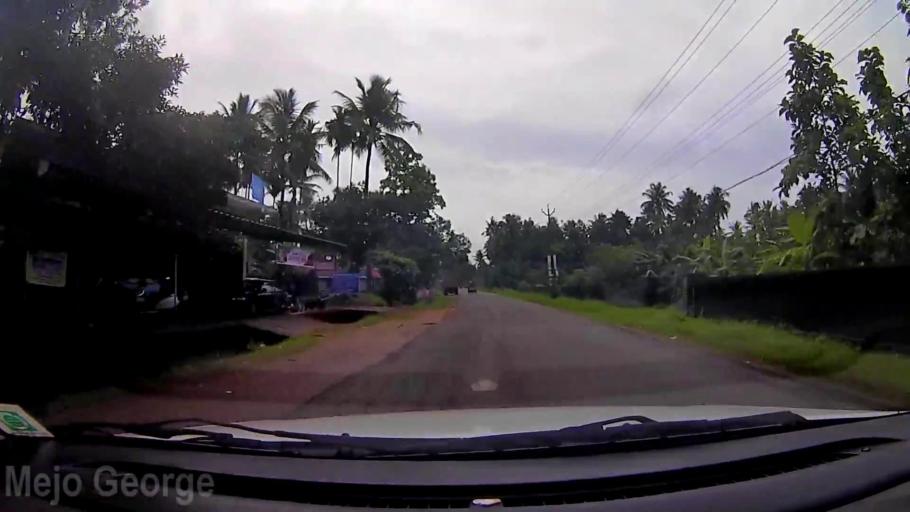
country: IN
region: Kerala
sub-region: Thrissur District
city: Kizhake Chalakudi
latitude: 10.3308
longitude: 76.3164
